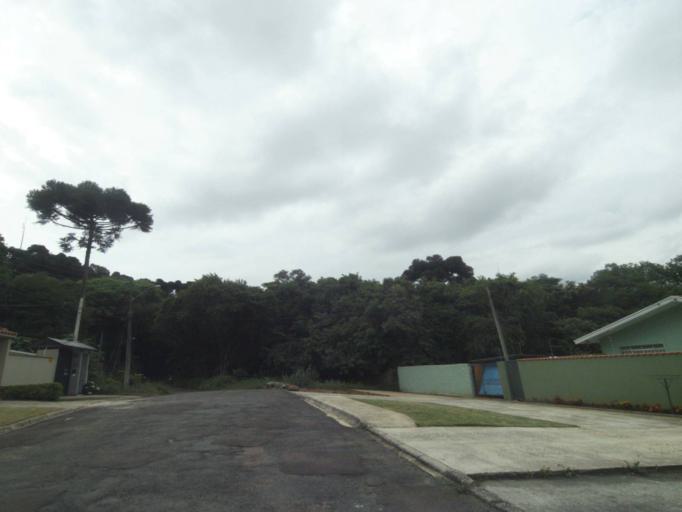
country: BR
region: Parana
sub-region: Curitiba
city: Curitiba
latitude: -25.3999
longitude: -49.2846
